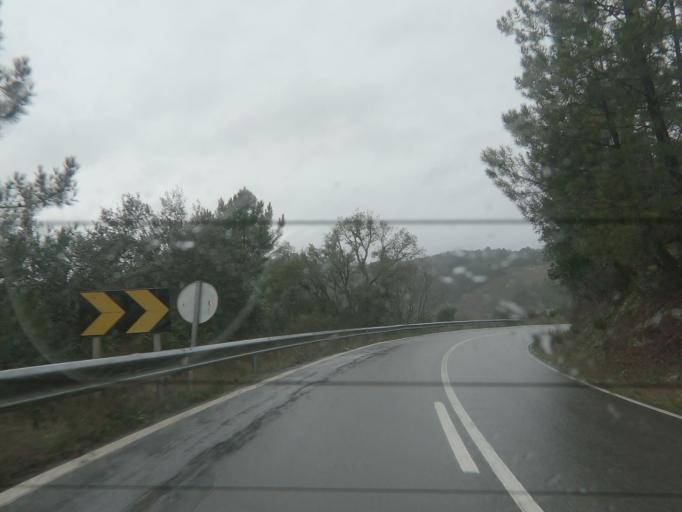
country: PT
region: Vila Real
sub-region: Vila Real
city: Vila Real
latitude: 41.2472
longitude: -7.6864
